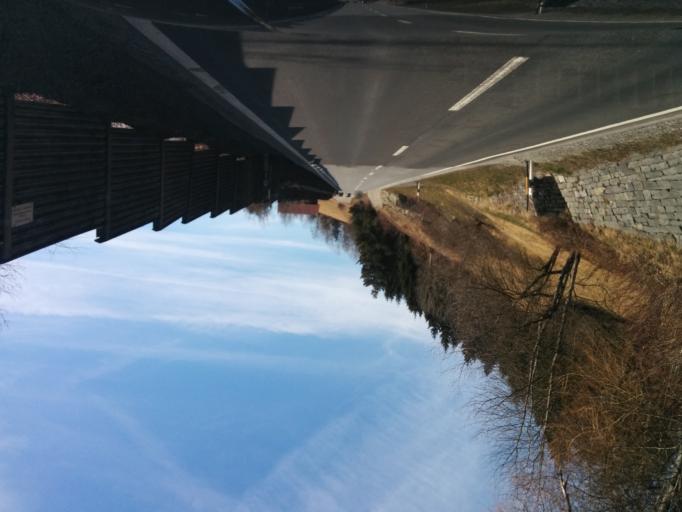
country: CH
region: Grisons
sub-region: Surselva District
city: Laax
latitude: 46.7897
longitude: 9.2328
